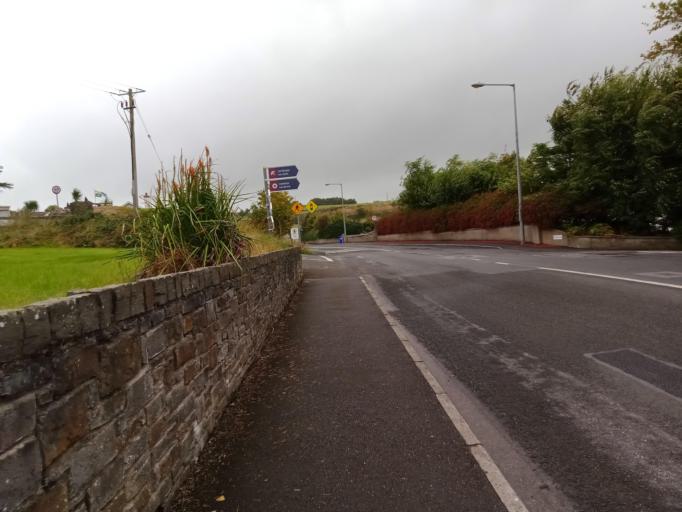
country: IE
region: Munster
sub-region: Waterford
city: Dungarvan
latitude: 52.0473
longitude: -7.5660
